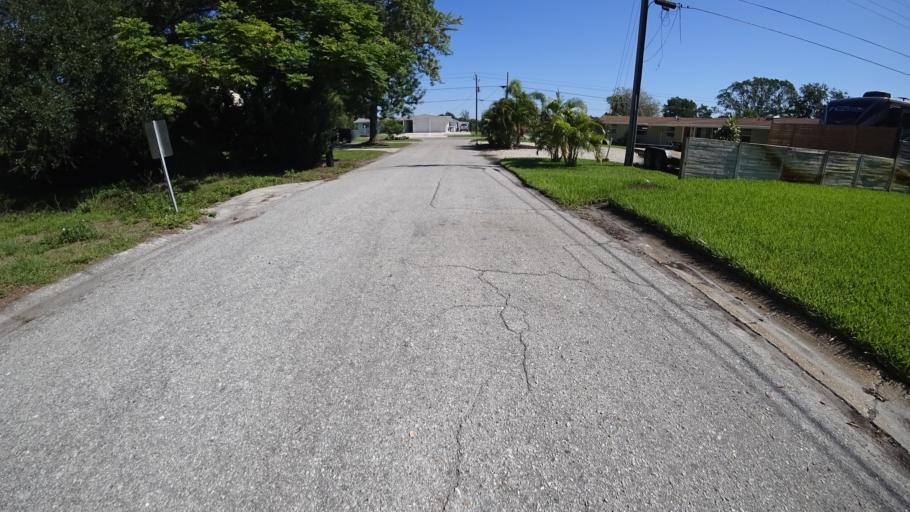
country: US
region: Florida
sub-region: Manatee County
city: West Bradenton
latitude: 27.4769
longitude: -82.6093
